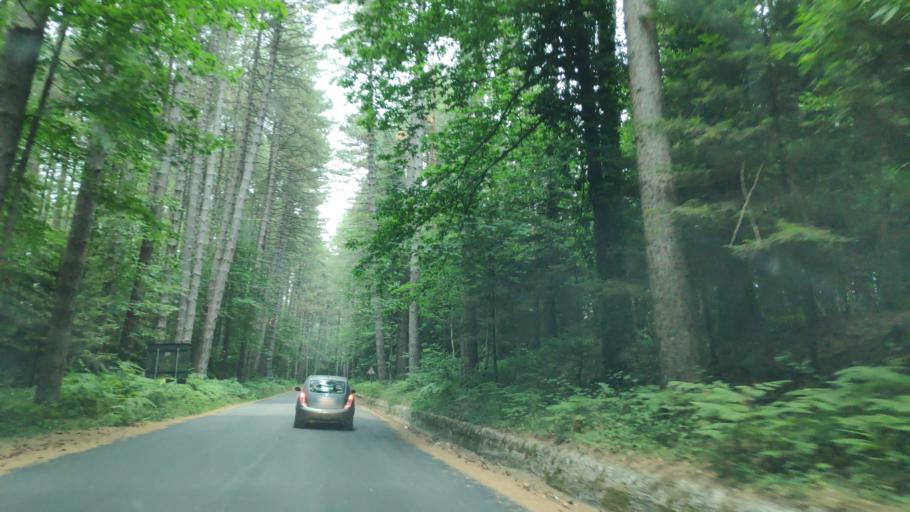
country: IT
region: Calabria
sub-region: Provincia di Vibo-Valentia
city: Mongiana
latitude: 38.5213
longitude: 16.3193
